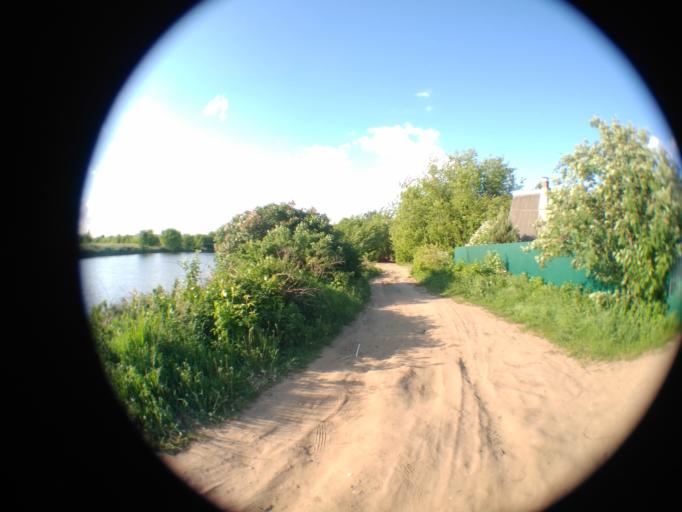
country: RU
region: Moskovskaya
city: Zhukovskiy
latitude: 55.5791
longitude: 38.1026
